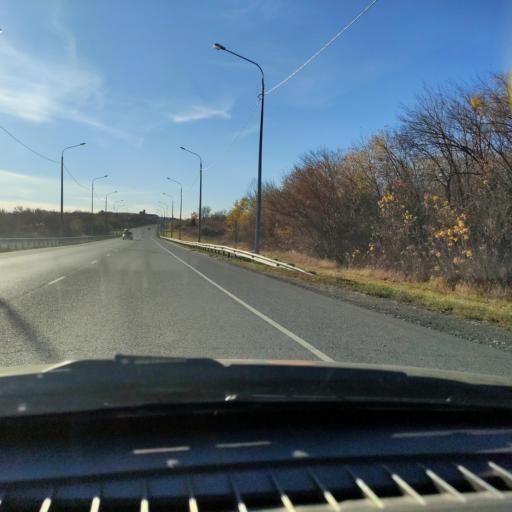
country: RU
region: Samara
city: Mezhdurechensk
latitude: 53.2500
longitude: 49.0250
